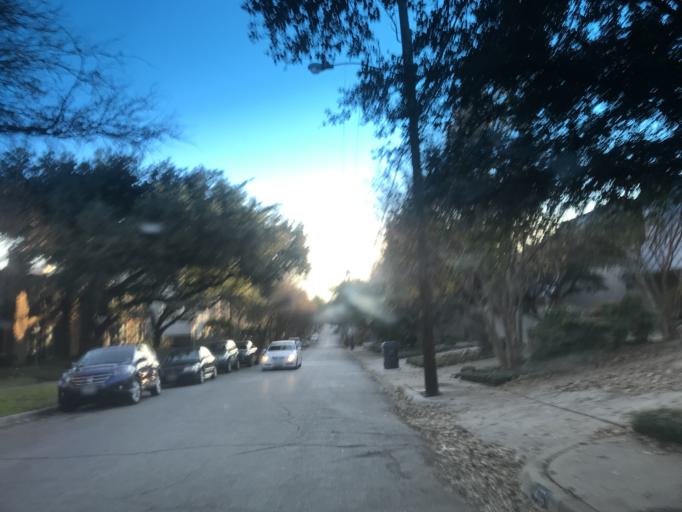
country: US
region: Texas
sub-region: Dallas County
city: Highland Park
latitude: 32.8147
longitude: -96.7951
